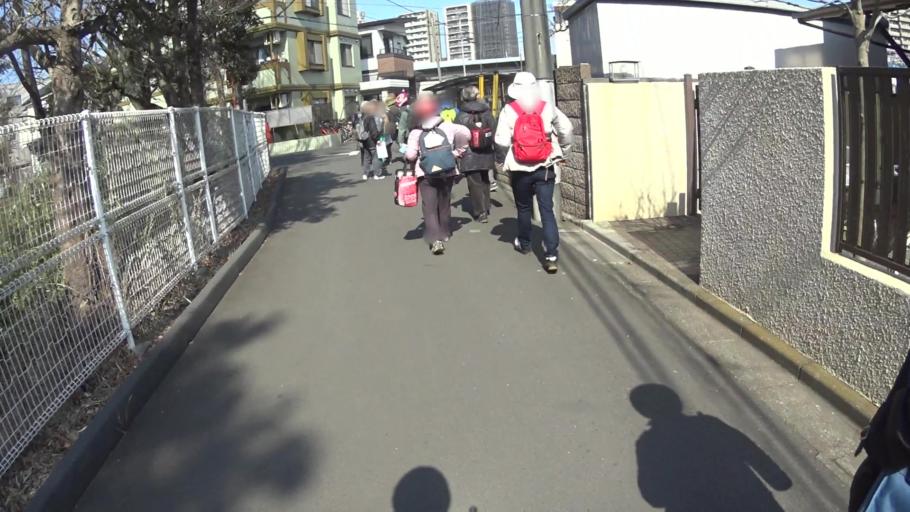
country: JP
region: Tokyo
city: Kokubunji
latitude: 35.6678
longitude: 139.4859
